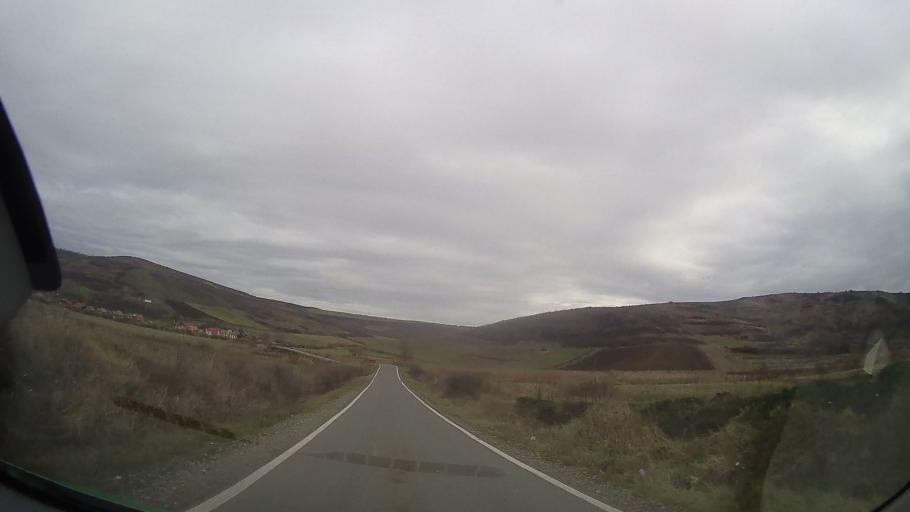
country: RO
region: Mures
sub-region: Comuna Faragau
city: Faragau
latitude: 46.7727
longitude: 24.5567
